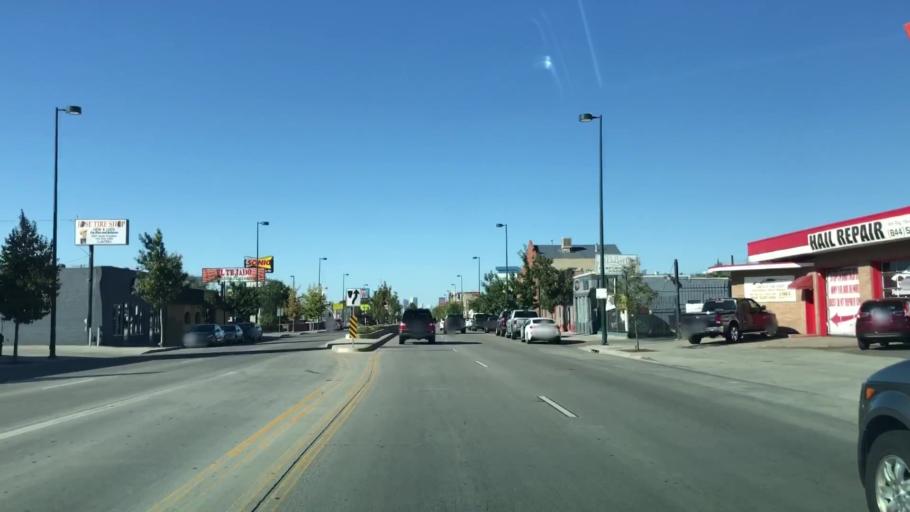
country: US
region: Colorado
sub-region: Arapahoe County
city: Englewood
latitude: 39.6679
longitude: -104.9876
